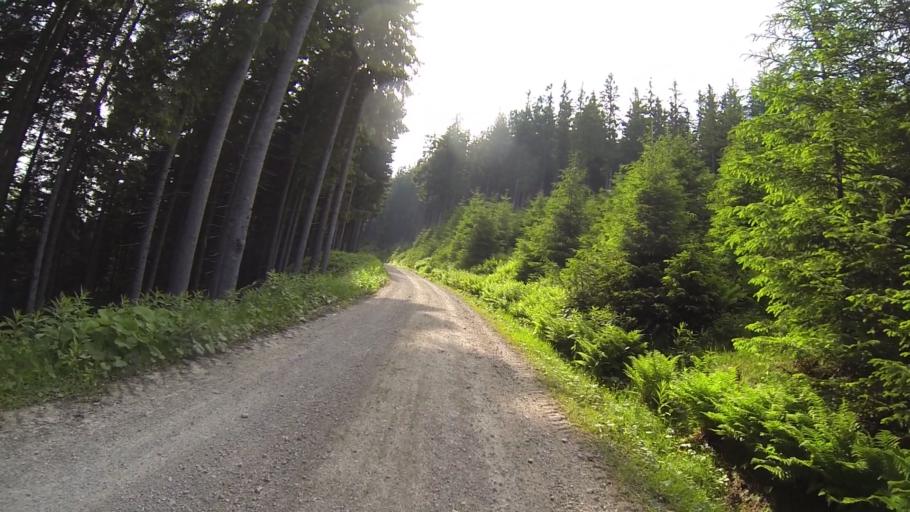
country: DE
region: Bavaria
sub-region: Swabia
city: Nesselwang
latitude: 47.5899
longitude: 10.5040
